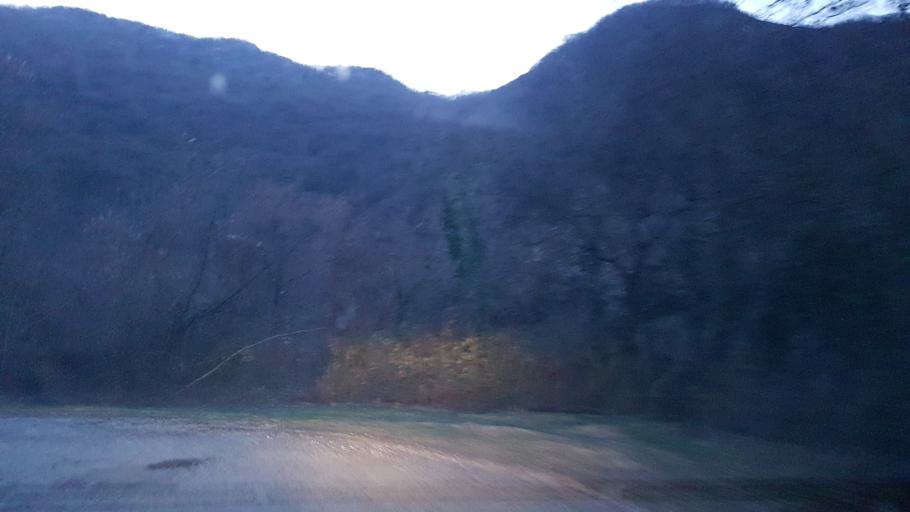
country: IT
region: Friuli Venezia Giulia
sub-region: Provincia di Udine
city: Gemona
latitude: 46.2836
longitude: 13.1510
